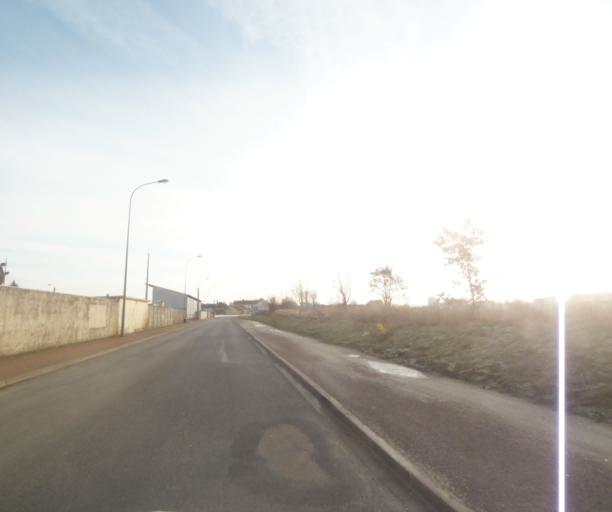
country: FR
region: Champagne-Ardenne
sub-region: Departement de la Haute-Marne
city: Saint-Dizier
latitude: 48.6455
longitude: 4.9419
